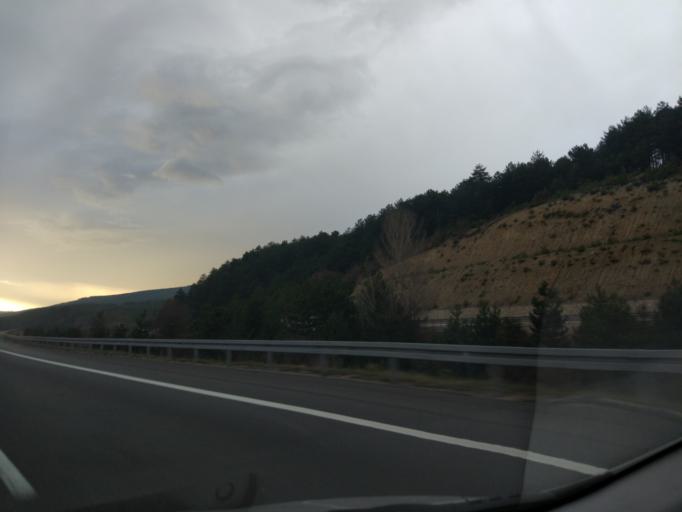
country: TR
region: Bolu
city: Yenicaga
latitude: 40.7488
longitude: 31.8942
